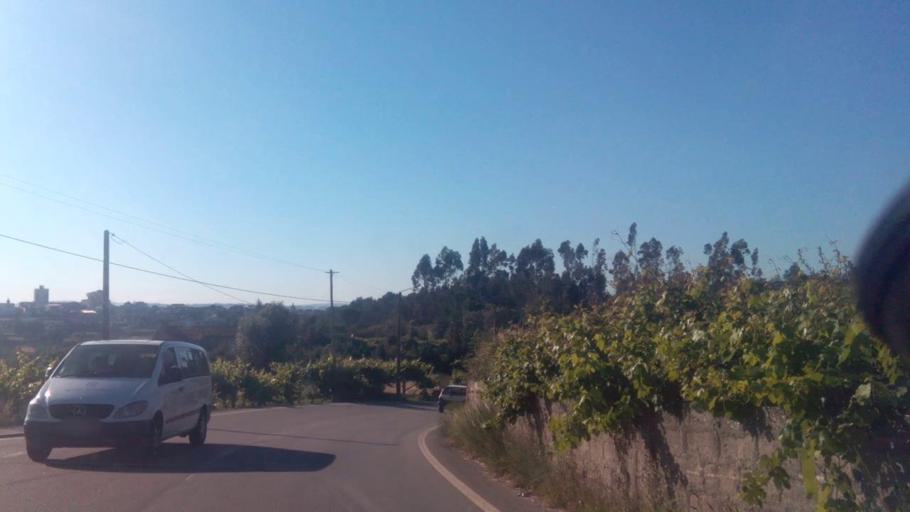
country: PT
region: Porto
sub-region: Penafiel
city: Penafiel
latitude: 41.1977
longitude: -8.2748
